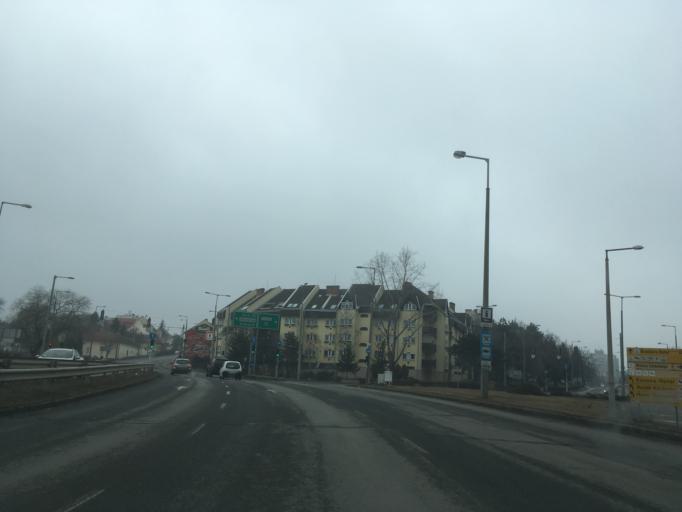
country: HU
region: Heves
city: Eger
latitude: 47.8909
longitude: 20.3796
